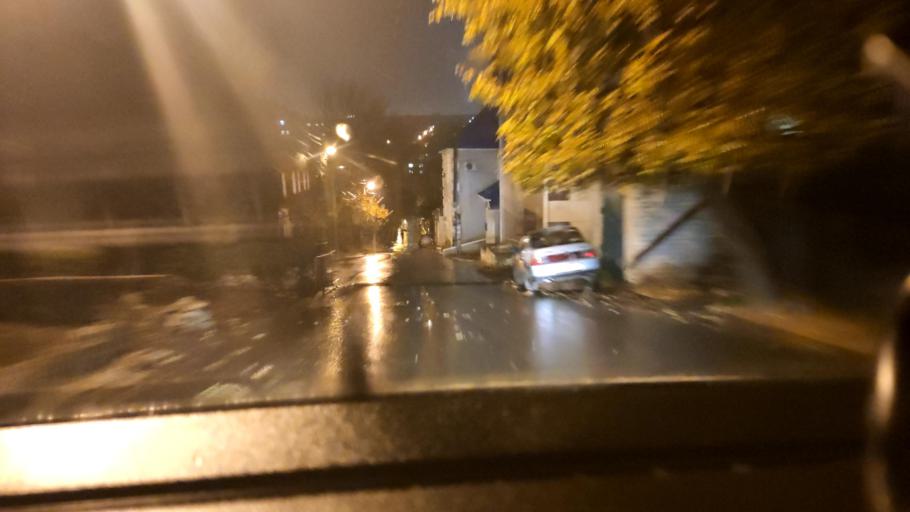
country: RU
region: Voronezj
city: Voronezh
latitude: 51.6563
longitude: 39.2031
